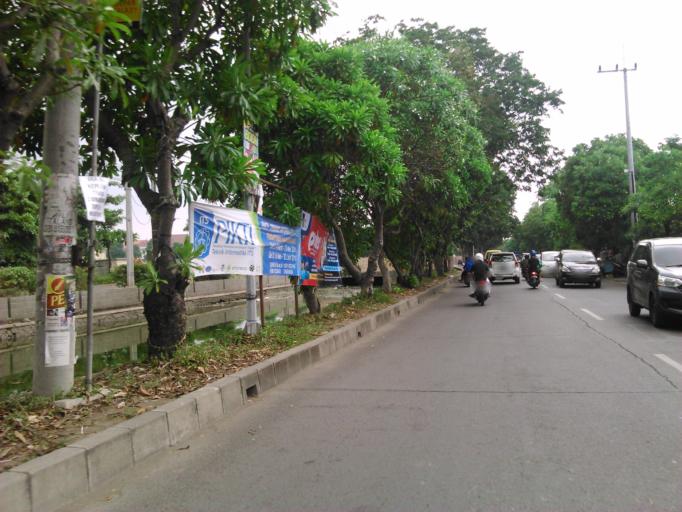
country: ID
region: East Java
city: Wonorejo
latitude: -7.2906
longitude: 112.7942
